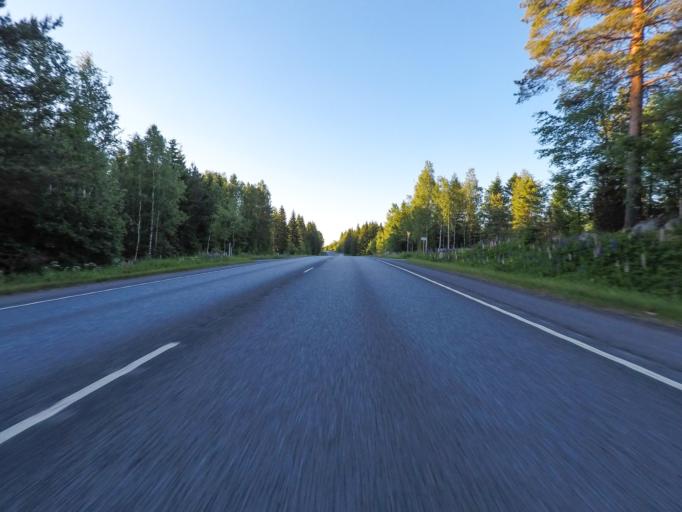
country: FI
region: Southern Savonia
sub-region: Mikkeli
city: Ristiina
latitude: 61.6167
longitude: 27.0521
